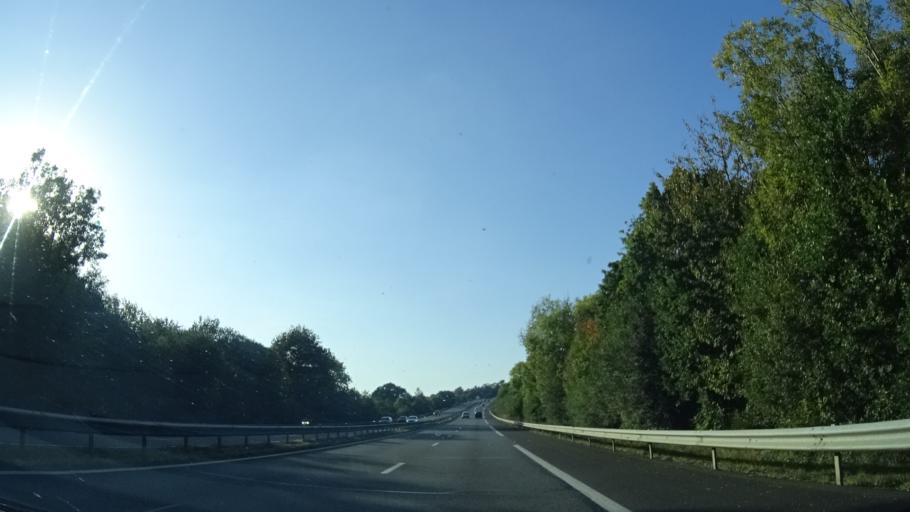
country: FR
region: Brittany
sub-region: Departement du Finistere
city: Le Faou
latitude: 48.3138
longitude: -4.2085
